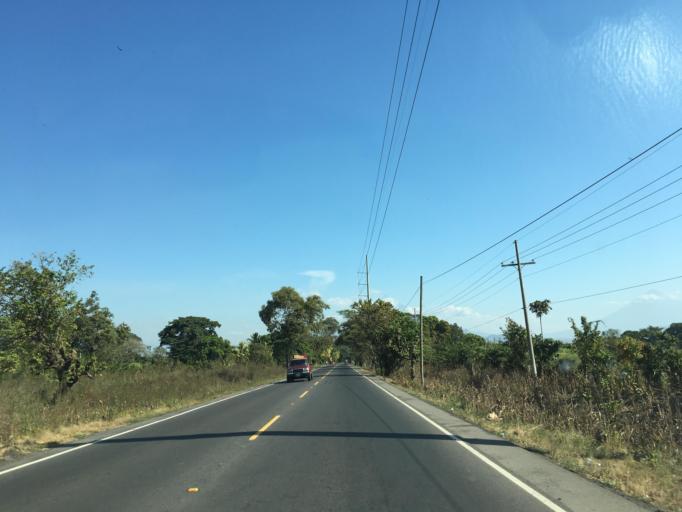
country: GT
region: Escuintla
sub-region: Municipio de La Democracia
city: La Democracia
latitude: 14.2082
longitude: -90.9573
